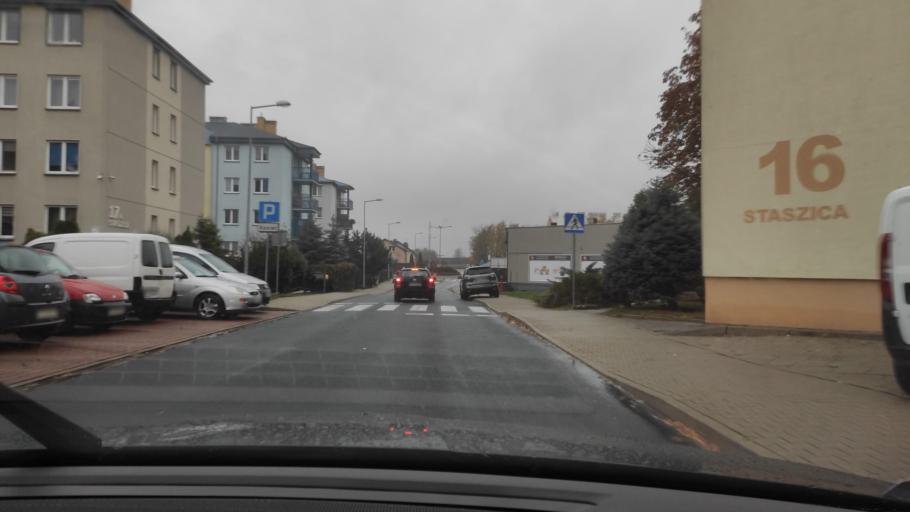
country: PL
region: Greater Poland Voivodeship
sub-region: Powiat poznanski
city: Kornik
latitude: 52.2537
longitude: 17.0879
